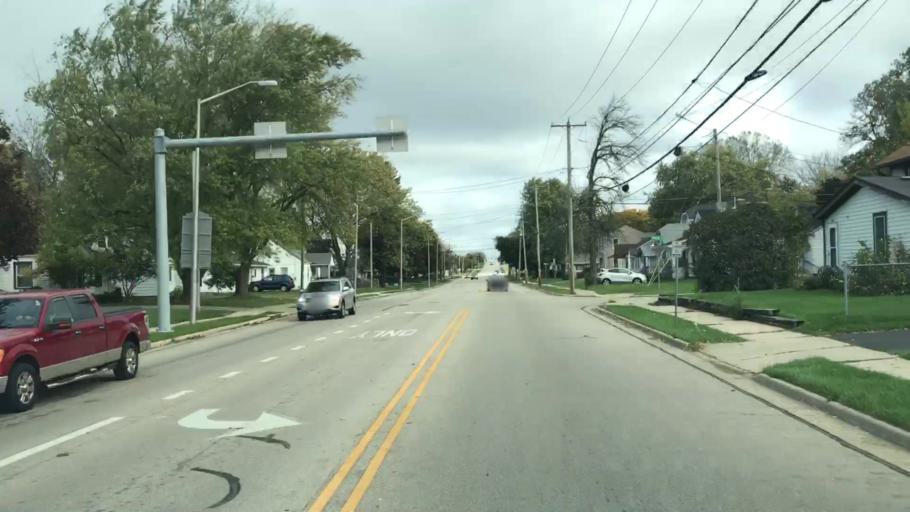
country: US
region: Wisconsin
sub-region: Waukesha County
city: Waukesha
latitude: 43.0237
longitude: -88.2260
